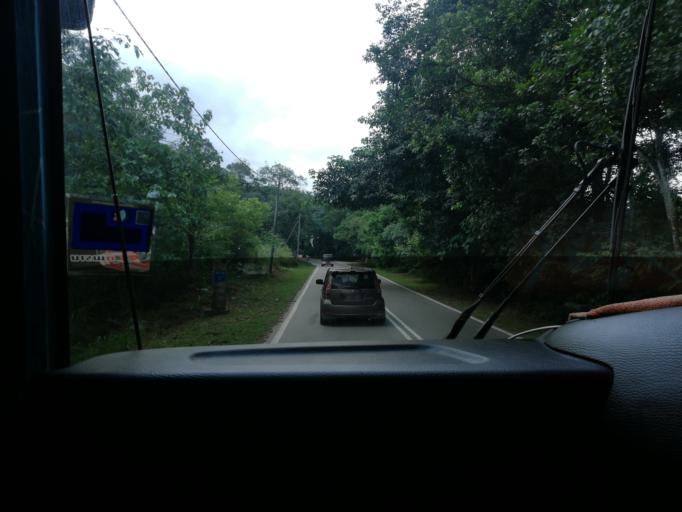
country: MY
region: Kedah
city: Kulim
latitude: 5.3024
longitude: 100.6196
